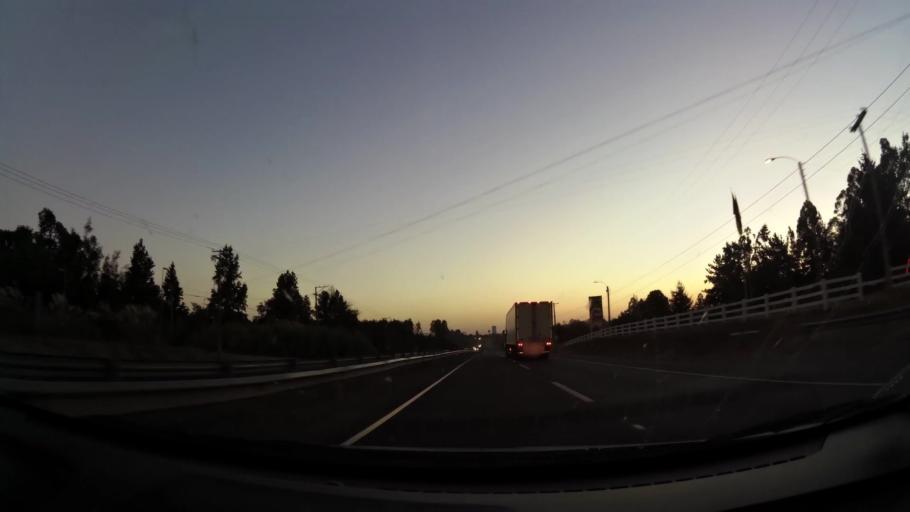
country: CL
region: Maule
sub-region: Provincia de Linares
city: Parral
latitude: -36.0854
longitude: -71.7895
